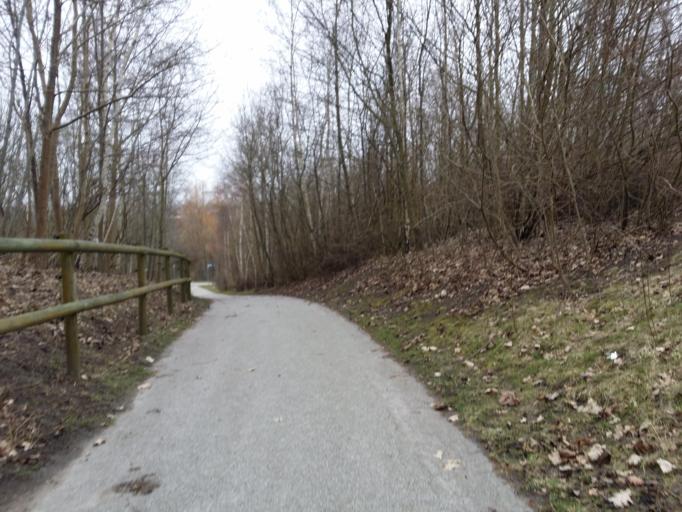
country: SE
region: Skane
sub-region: Burlovs Kommun
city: Arloev
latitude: 55.6057
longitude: 13.0853
